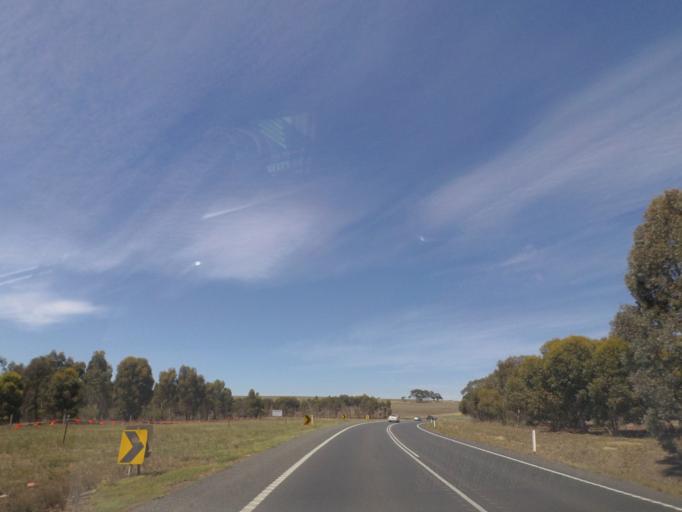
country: AU
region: Victoria
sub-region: Greater Geelong
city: Lara
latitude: -37.8839
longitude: 144.3782
